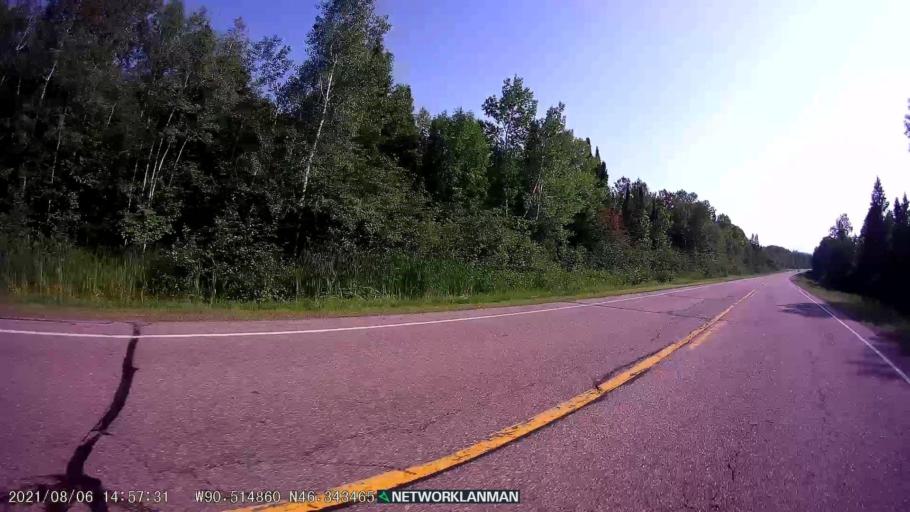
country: US
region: Wisconsin
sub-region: Iron County
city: Hurley
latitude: 46.3431
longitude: -90.5153
